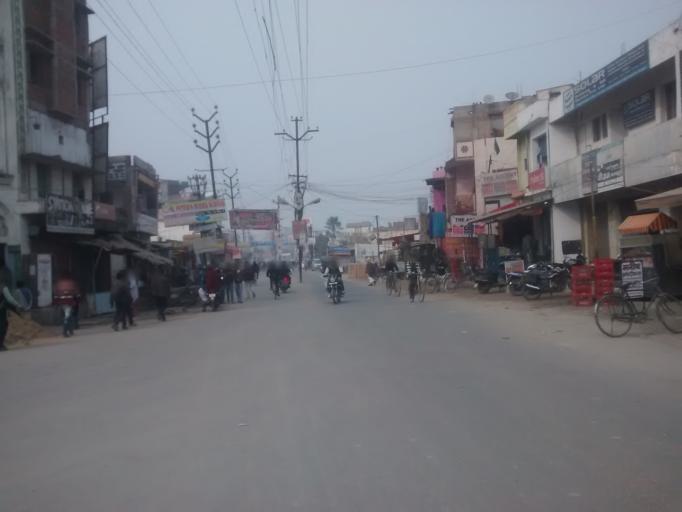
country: IN
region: Bihar
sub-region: Muzaffarpur
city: Muzaffarpur
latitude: 26.1044
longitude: 85.3991
